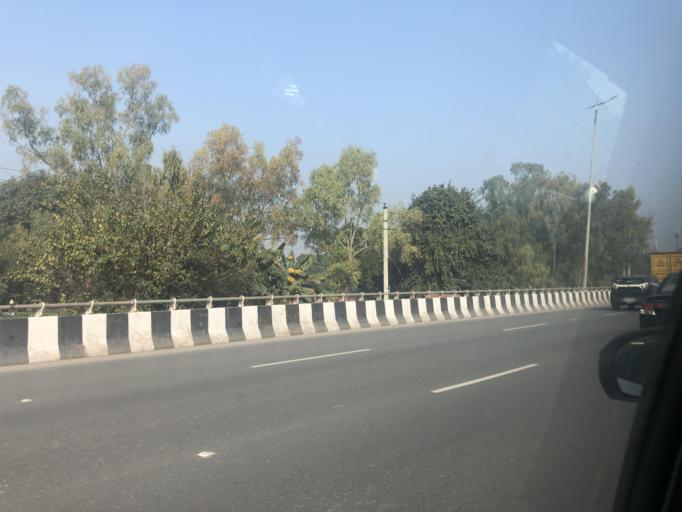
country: IN
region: Haryana
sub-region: Gurgaon
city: Gurgaon
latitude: 28.5191
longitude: 77.0965
